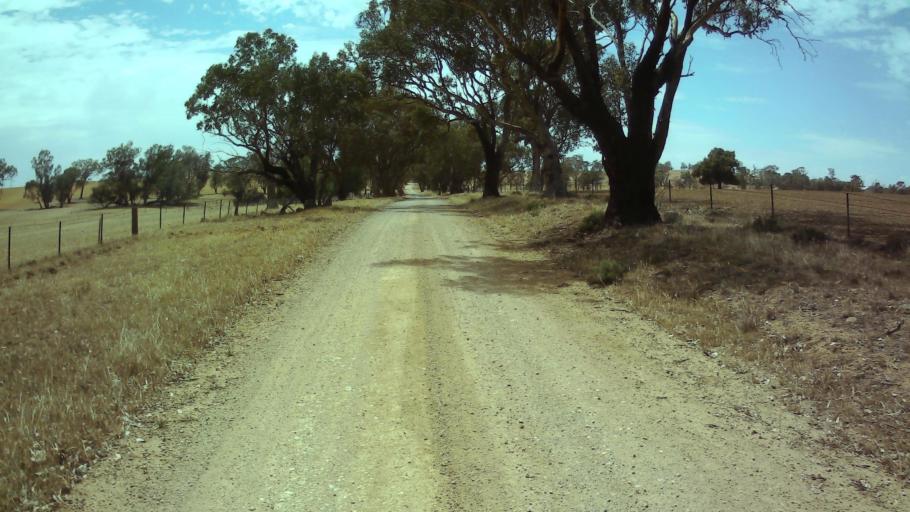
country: AU
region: New South Wales
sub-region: Cowra
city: Cowra
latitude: -33.9283
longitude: 148.4589
